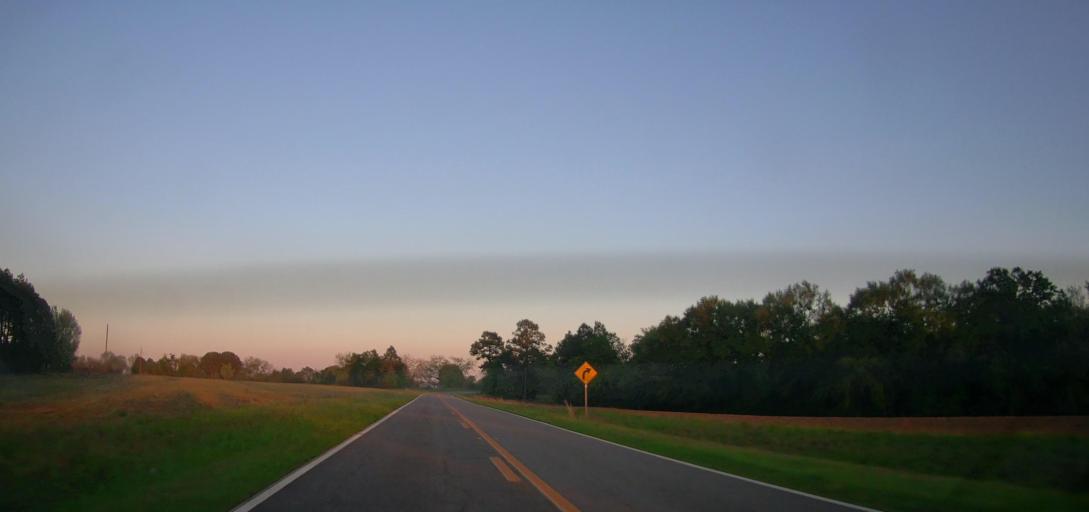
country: US
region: Georgia
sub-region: Wilcox County
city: Rochelle
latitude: 31.7925
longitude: -83.4388
